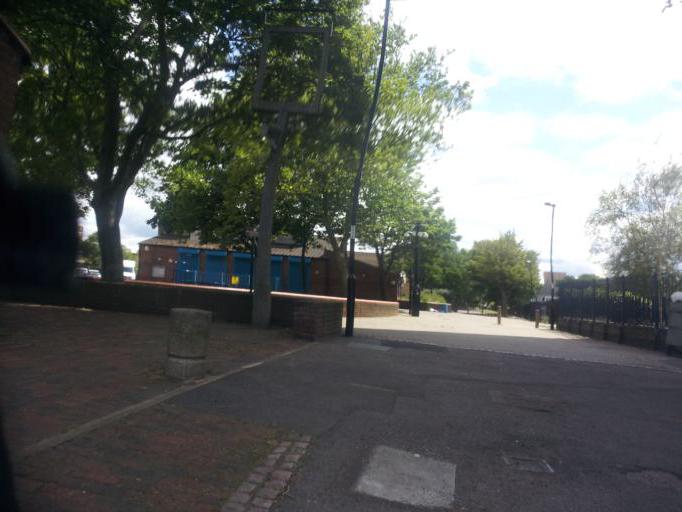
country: GB
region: England
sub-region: Greater London
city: Poplar
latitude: 51.4808
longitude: -0.0387
